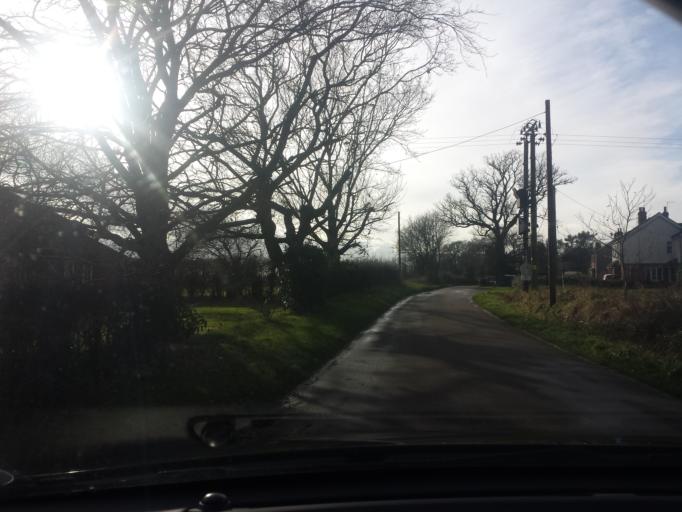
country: GB
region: England
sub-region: Essex
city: Alresford
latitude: 51.8990
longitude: 1.0314
